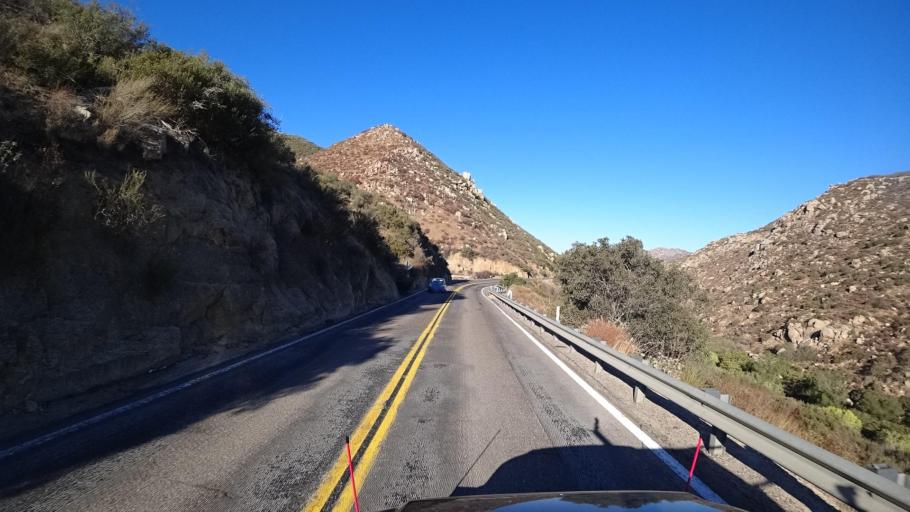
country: MX
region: Baja California
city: Tecate
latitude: 32.5949
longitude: -116.6713
